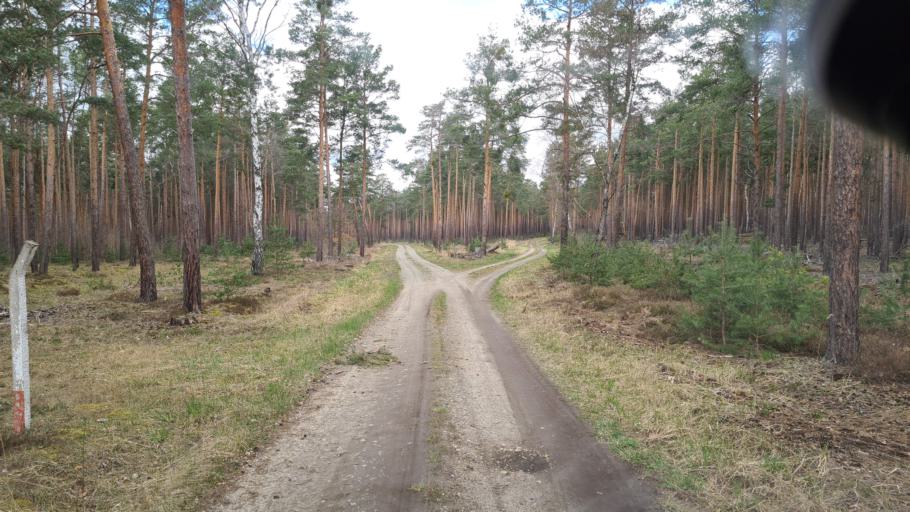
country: DE
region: Brandenburg
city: Schonborn
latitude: 51.6427
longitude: 13.4921
